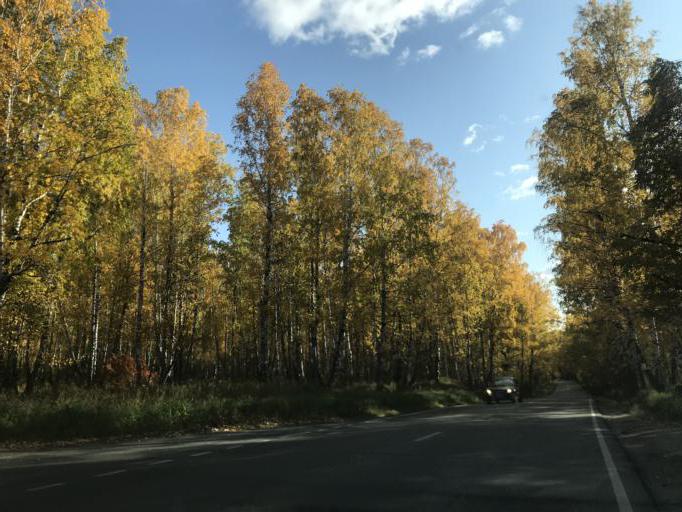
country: RU
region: Chelyabinsk
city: Dolgoderevenskoye
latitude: 55.2746
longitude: 61.3648
